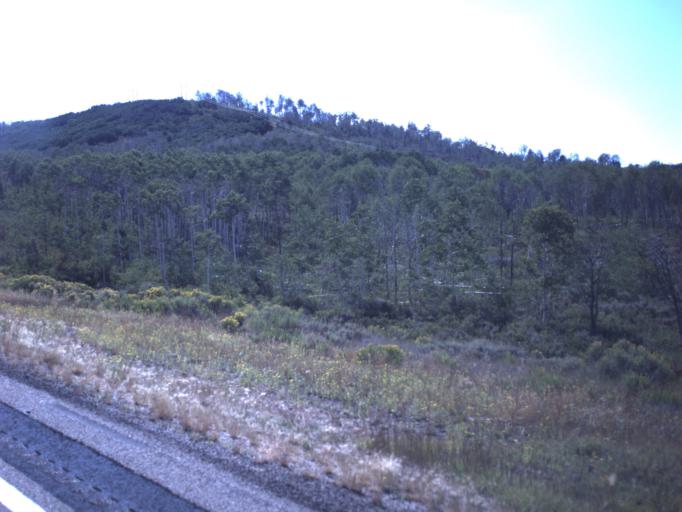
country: US
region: Utah
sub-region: Summit County
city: Francis
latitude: 40.1908
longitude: -111.0152
